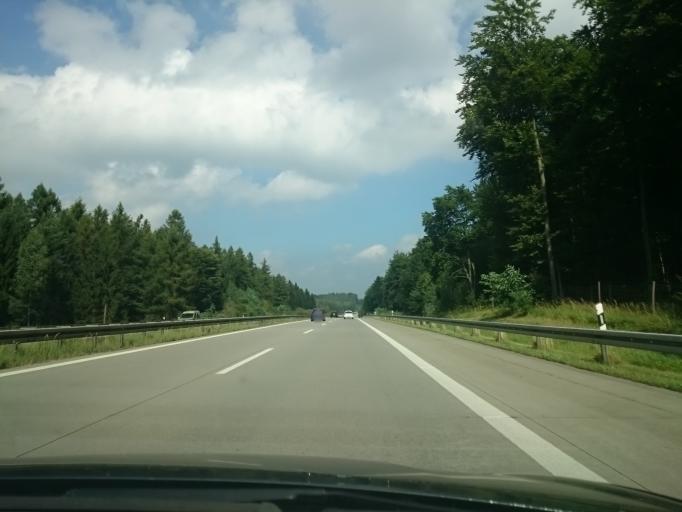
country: DE
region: Brandenburg
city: Bernau bei Berlin
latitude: 52.7455
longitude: 13.5419
